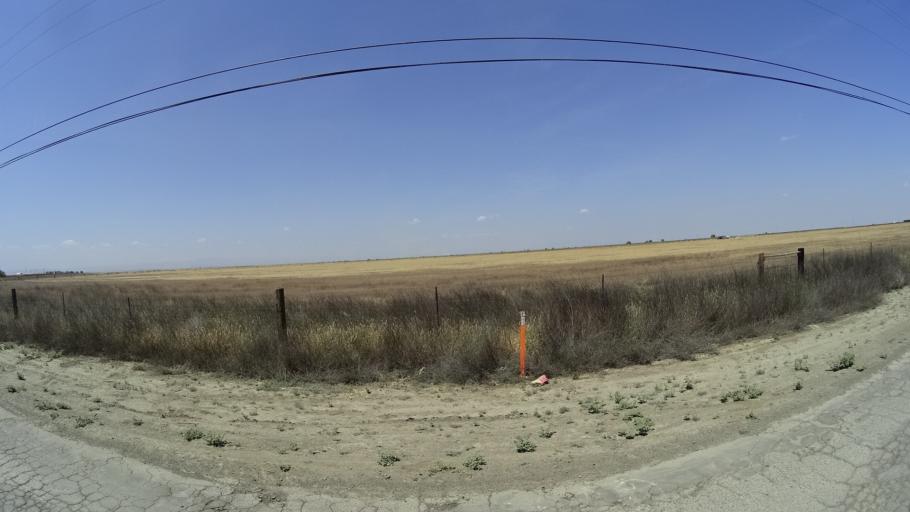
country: US
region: California
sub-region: Kings County
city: Stratford
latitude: 36.1620
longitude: -119.8517
